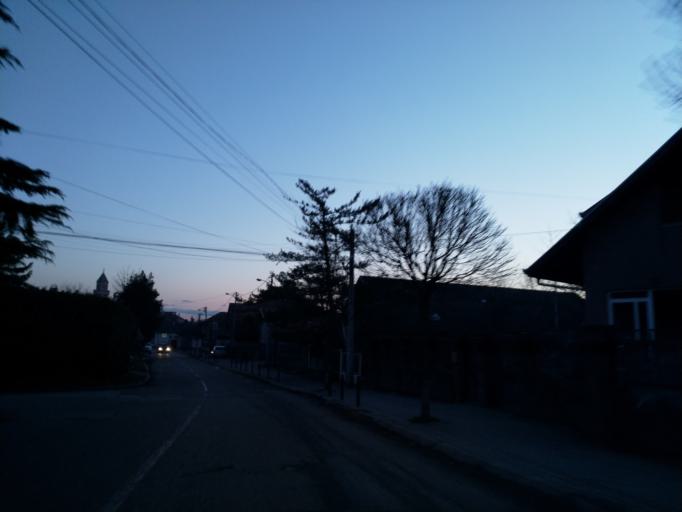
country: RS
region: Central Serbia
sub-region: Pomoravski Okrug
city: Paracin
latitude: 43.8670
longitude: 21.4137
